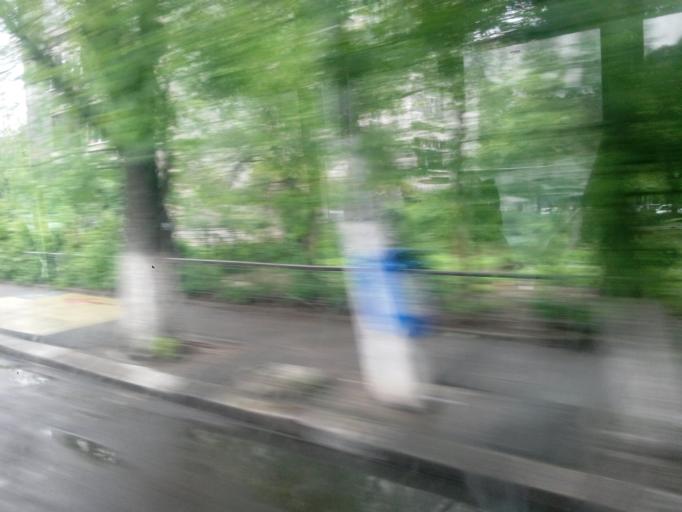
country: RO
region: Ilfov
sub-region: Comuna Fundeni-Dobroesti
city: Fundeni
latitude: 44.4472
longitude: 26.1375
